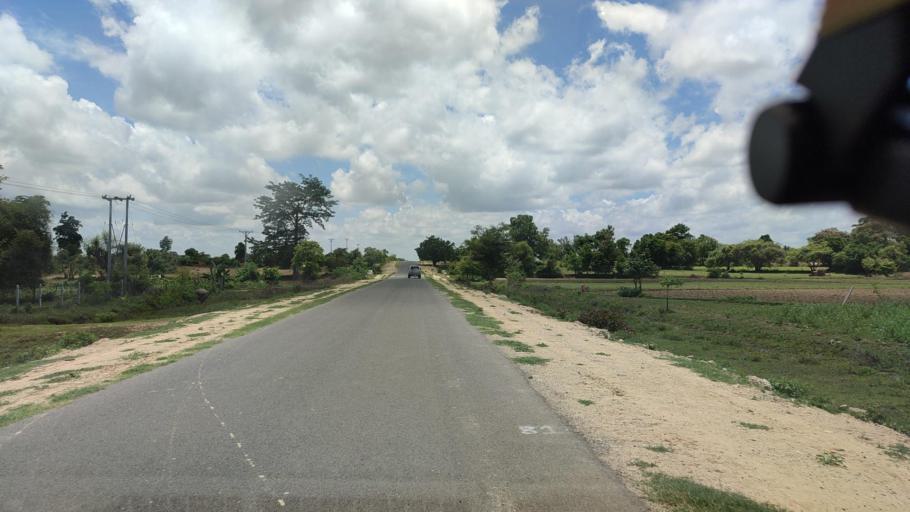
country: MM
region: Magway
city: Taungdwingyi
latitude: 20.1638
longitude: 95.5018
